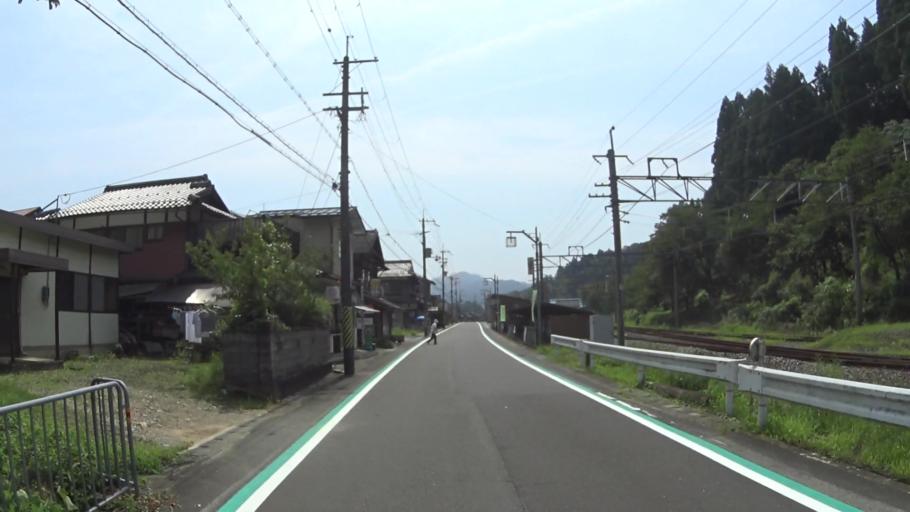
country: JP
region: Kyoto
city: Ayabe
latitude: 35.2138
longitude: 135.4213
